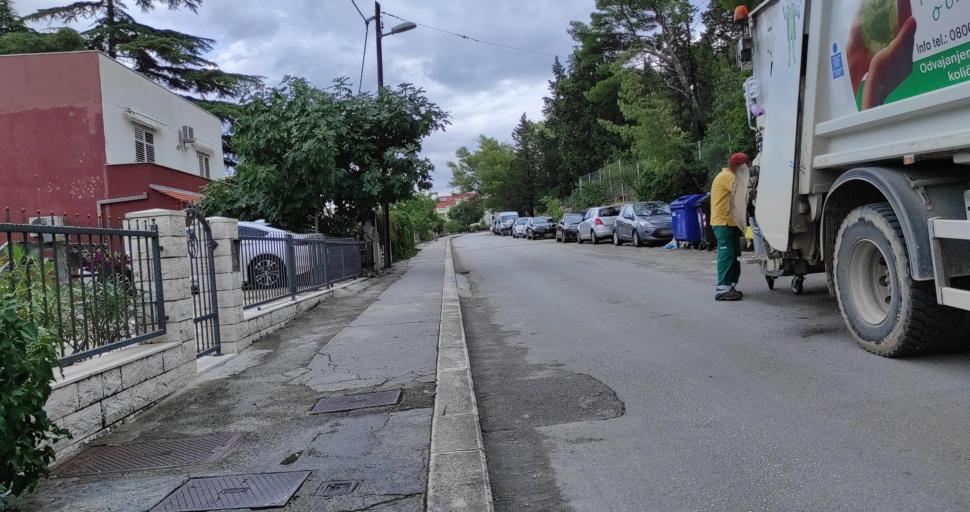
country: HR
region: Splitsko-Dalmatinska
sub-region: Grad Split
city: Split
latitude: 43.5128
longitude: 16.4246
